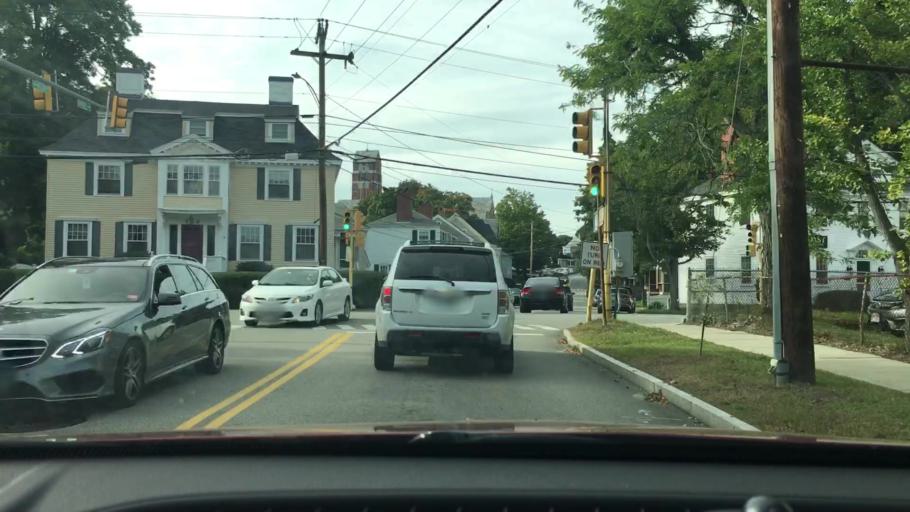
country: US
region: New Hampshire
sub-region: Rockingham County
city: Portsmouth
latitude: 43.0714
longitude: -70.7620
